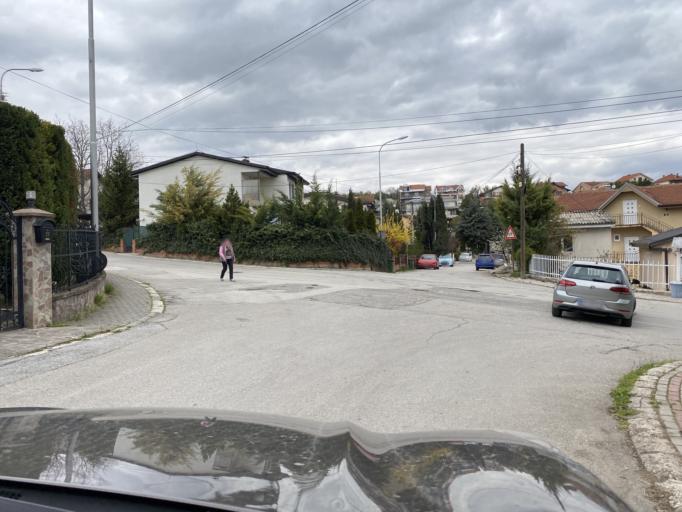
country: MK
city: Radishani
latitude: 42.0651
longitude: 21.4490
